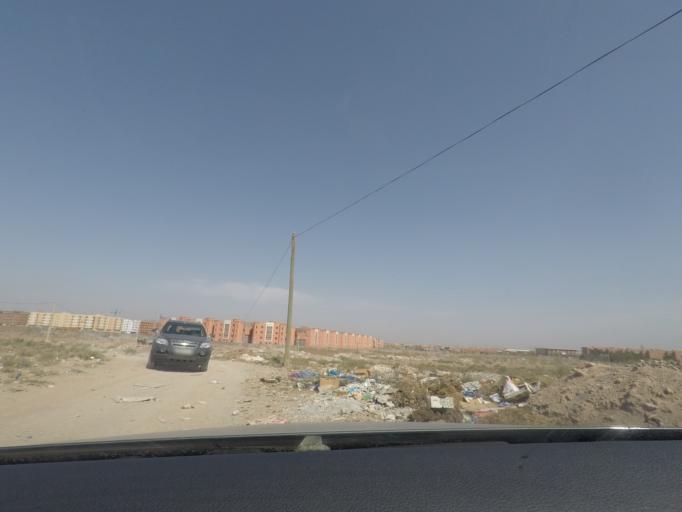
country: MA
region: Marrakech-Tensift-Al Haouz
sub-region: Marrakech
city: Marrakesh
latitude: 31.5829
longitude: -8.0285
